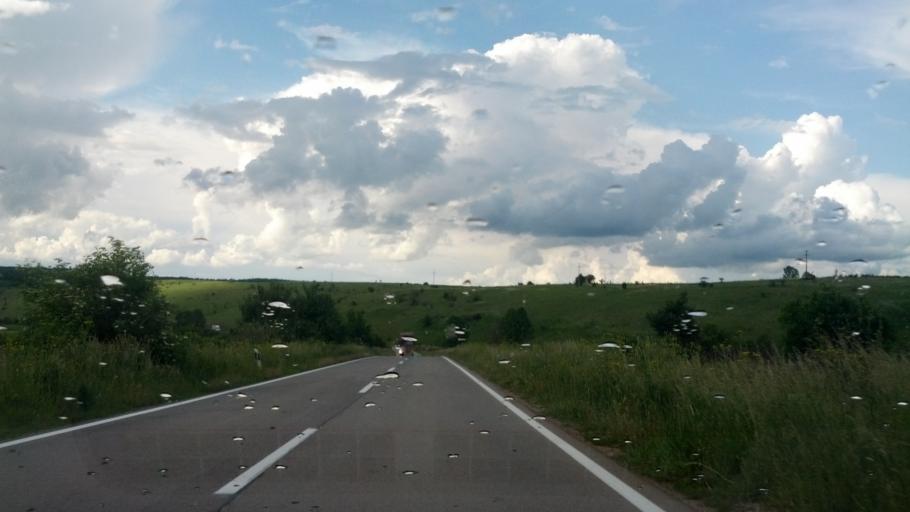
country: BA
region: Federation of Bosnia and Herzegovina
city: Izacic
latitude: 44.9108
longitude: 15.7188
